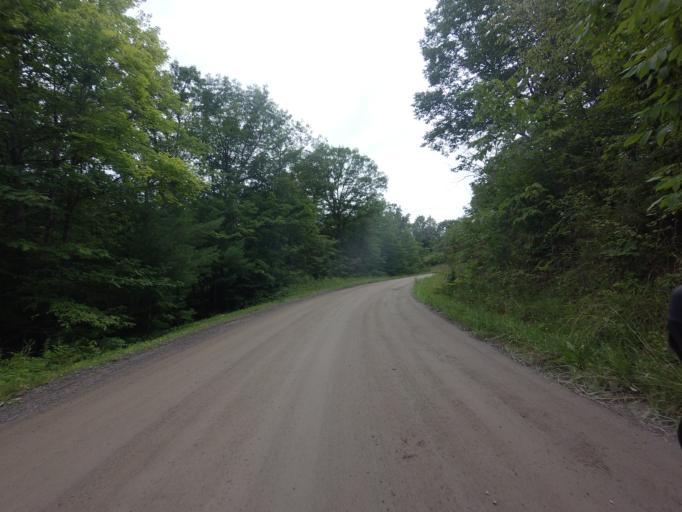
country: CA
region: Ontario
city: Kingston
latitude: 44.5533
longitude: -76.6159
